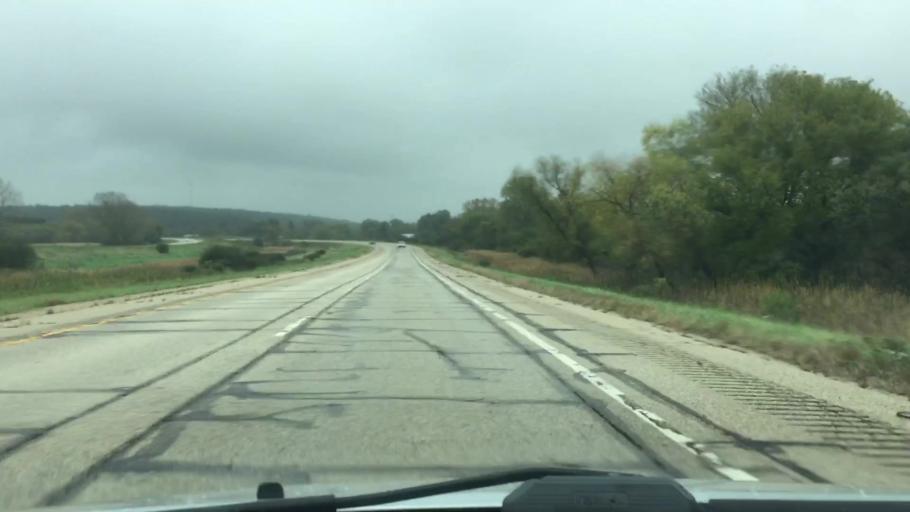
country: US
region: Wisconsin
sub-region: Walworth County
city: Como
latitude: 42.6206
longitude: -88.4622
